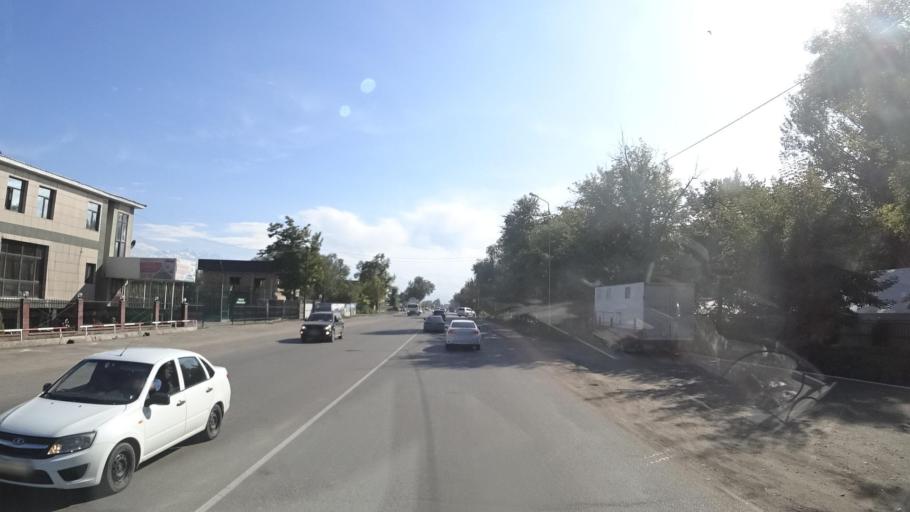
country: KZ
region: Almaty Oblysy
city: Energeticheskiy
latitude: 43.4251
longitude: 77.0245
